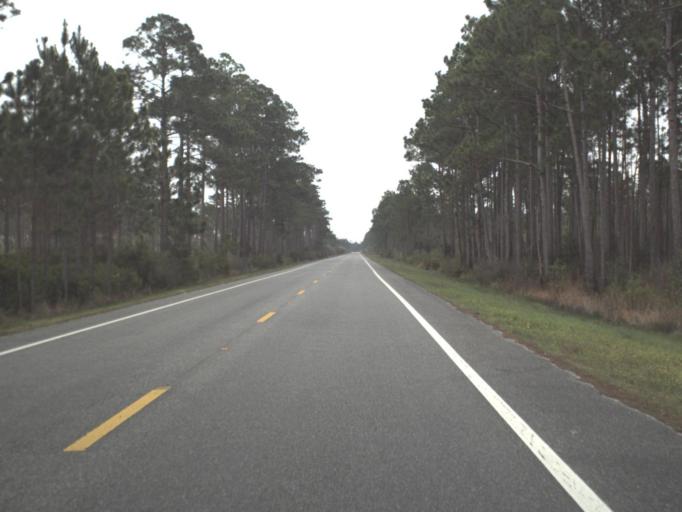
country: US
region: Florida
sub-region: Franklin County
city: Eastpoint
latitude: 29.8097
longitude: -84.8406
